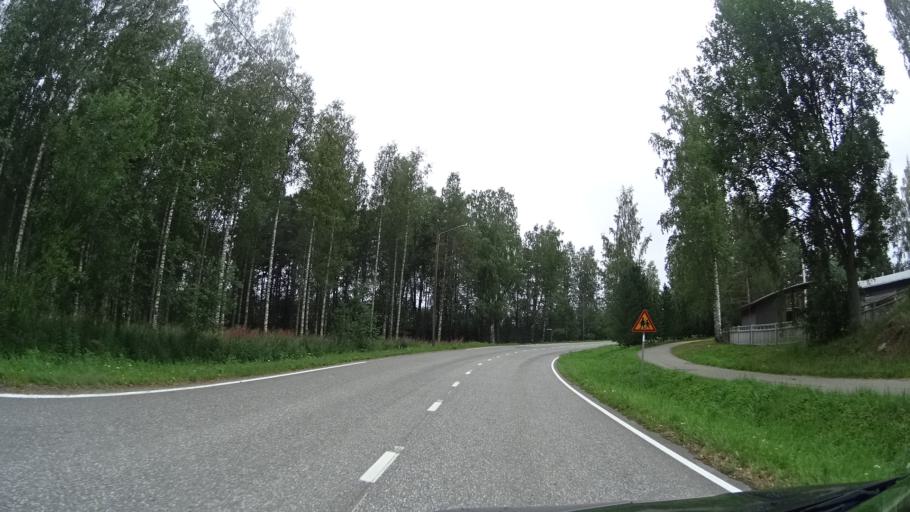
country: FI
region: Southern Savonia
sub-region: Savonlinna
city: Punkaharju
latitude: 61.7542
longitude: 29.3868
